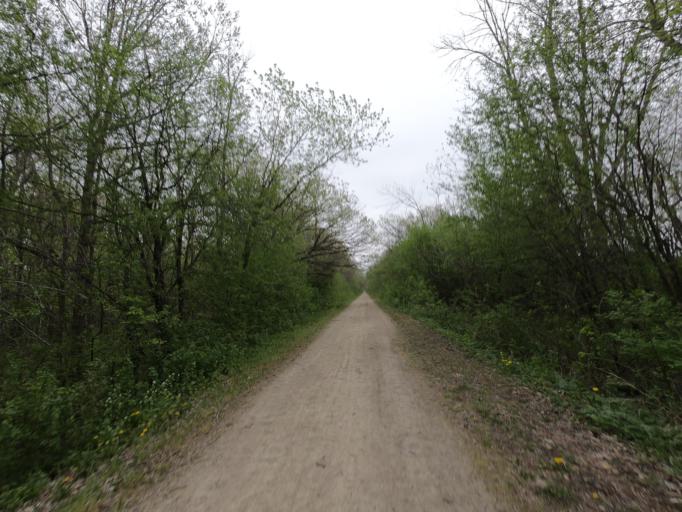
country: US
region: Wisconsin
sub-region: Jefferson County
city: Johnson Creek
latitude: 43.0344
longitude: -88.7552
